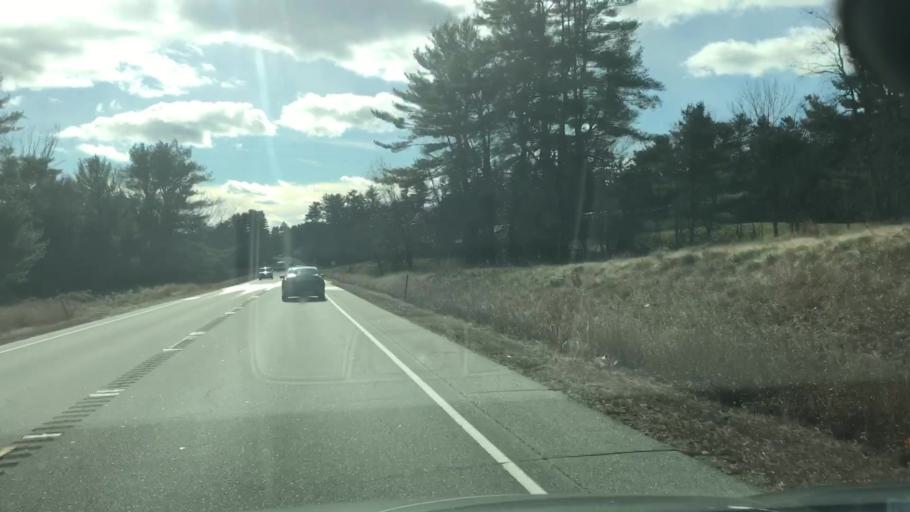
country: US
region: New Hampshire
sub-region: Merrimack County
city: Chichester
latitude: 43.2683
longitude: -71.3700
